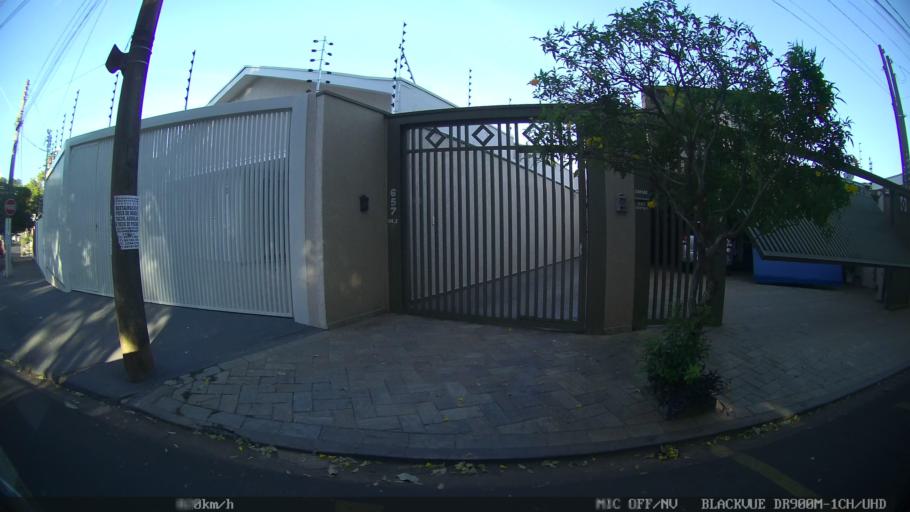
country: BR
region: Sao Paulo
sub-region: Sao Jose Do Rio Preto
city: Sao Jose do Rio Preto
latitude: -20.7985
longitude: -49.3628
